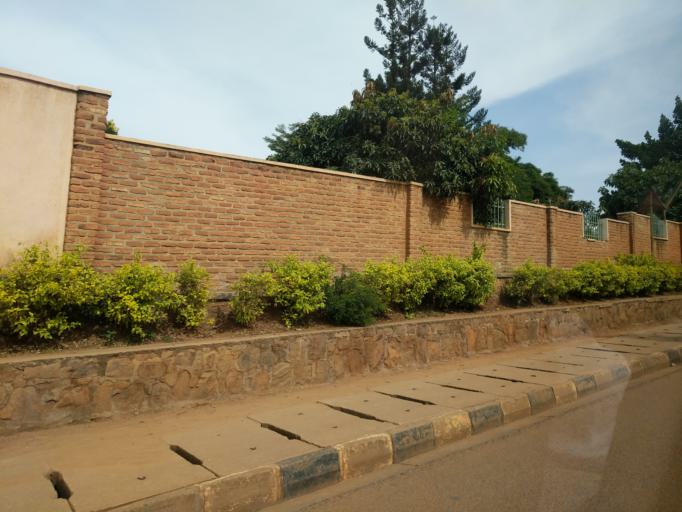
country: RW
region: Kigali
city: Kigali
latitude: -1.9739
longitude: 30.1348
